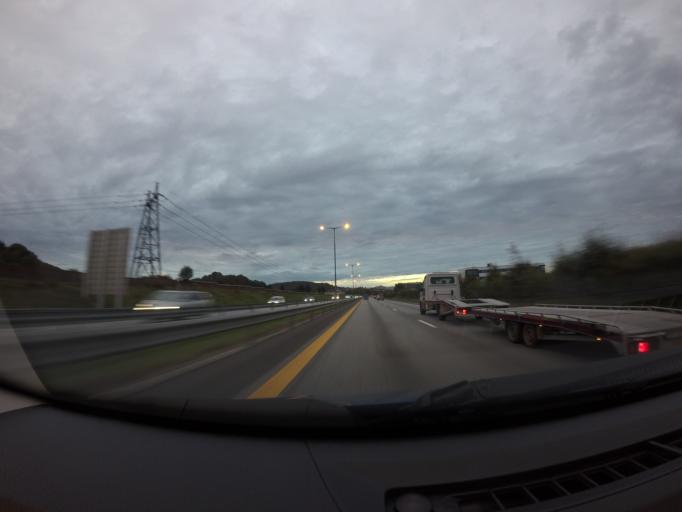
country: NO
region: Rogaland
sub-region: Sola
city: Sola
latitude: 58.9054
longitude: 5.7015
